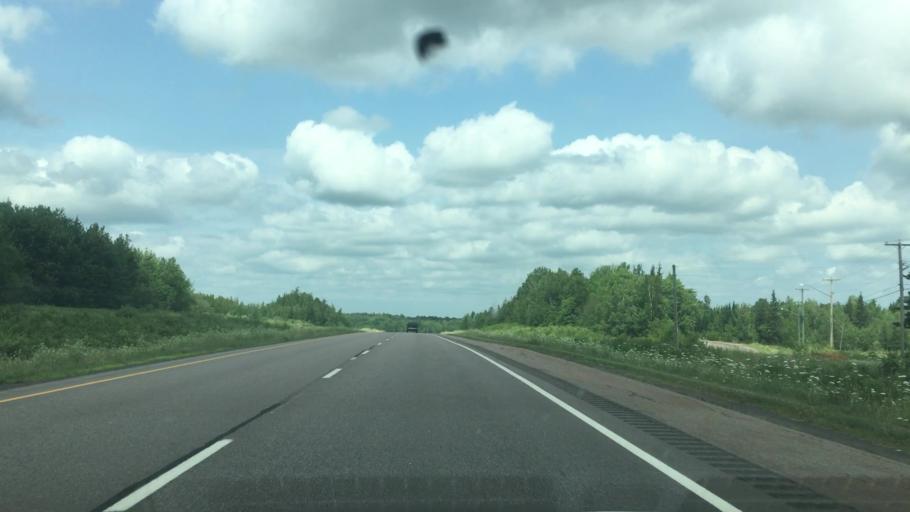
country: CA
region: New Brunswick
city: Dieppe
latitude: 46.0849
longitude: -64.5944
